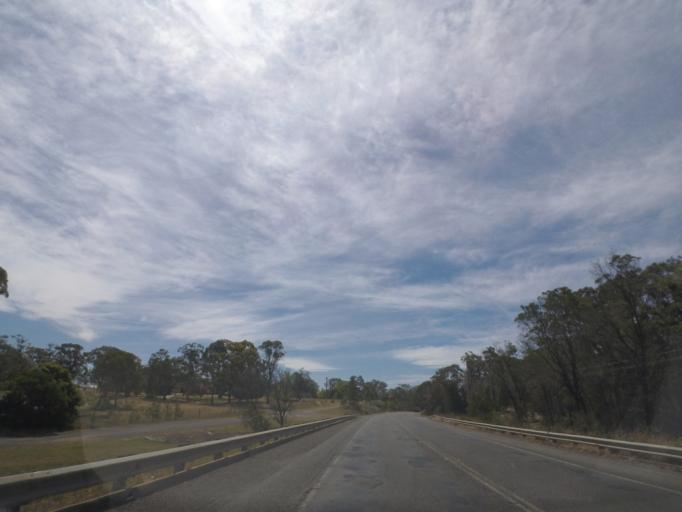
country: AU
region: New South Wales
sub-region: Wollondilly
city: Buxton
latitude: -34.2679
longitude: 150.5736
